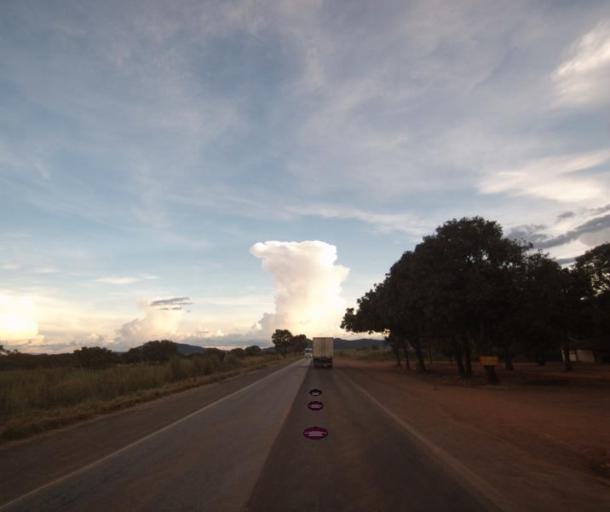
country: BR
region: Goias
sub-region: Uruacu
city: Uruacu
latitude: -14.3386
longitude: -49.1555
